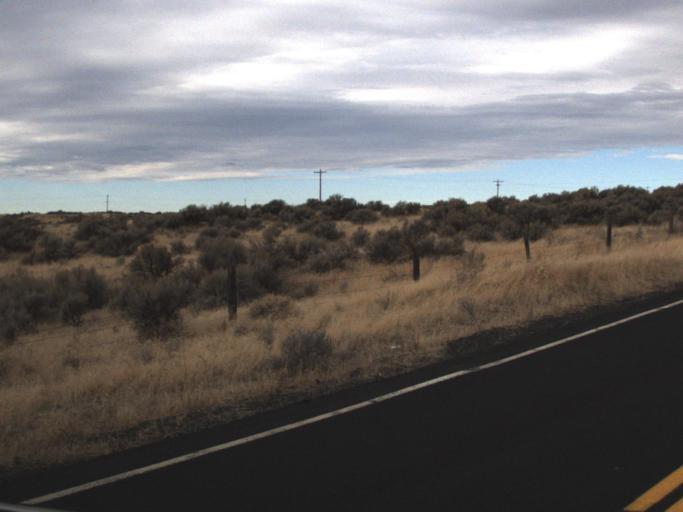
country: US
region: Washington
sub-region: Adams County
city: Ritzville
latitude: 47.4237
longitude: -118.6997
